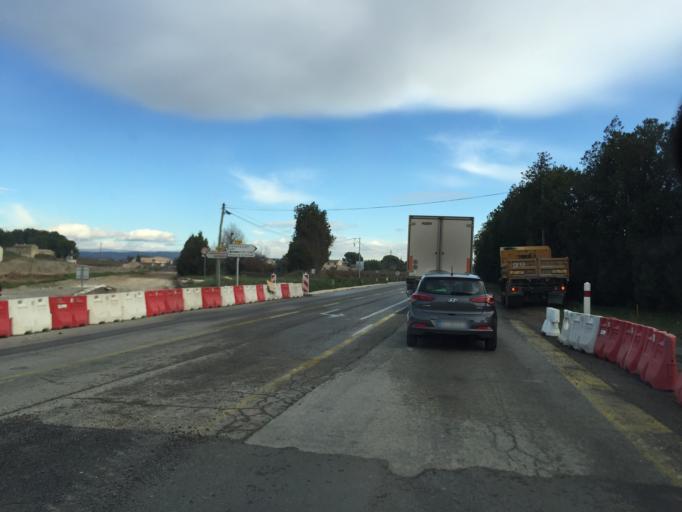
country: FR
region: Provence-Alpes-Cote d'Azur
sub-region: Departement du Vaucluse
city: Lagnes
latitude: 43.8691
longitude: 5.1260
